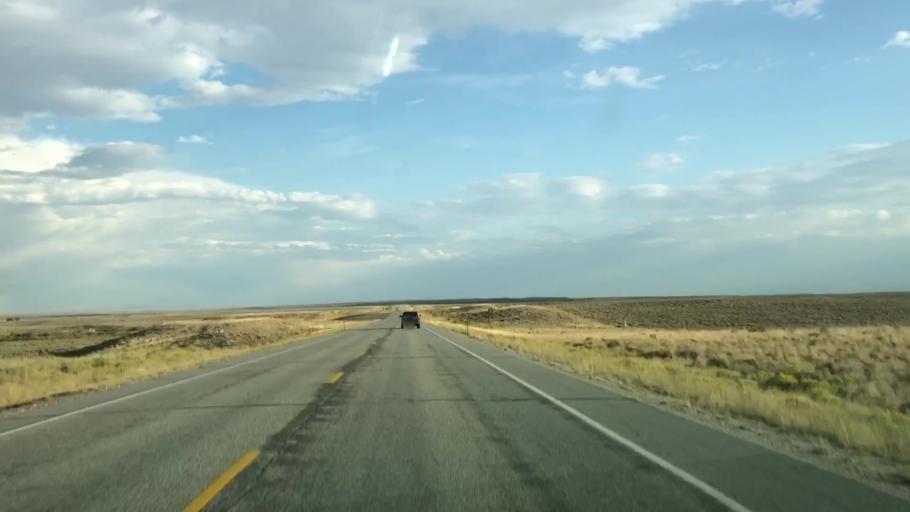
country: US
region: Wyoming
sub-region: Sublette County
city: Marbleton
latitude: 42.3304
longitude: -109.5157
